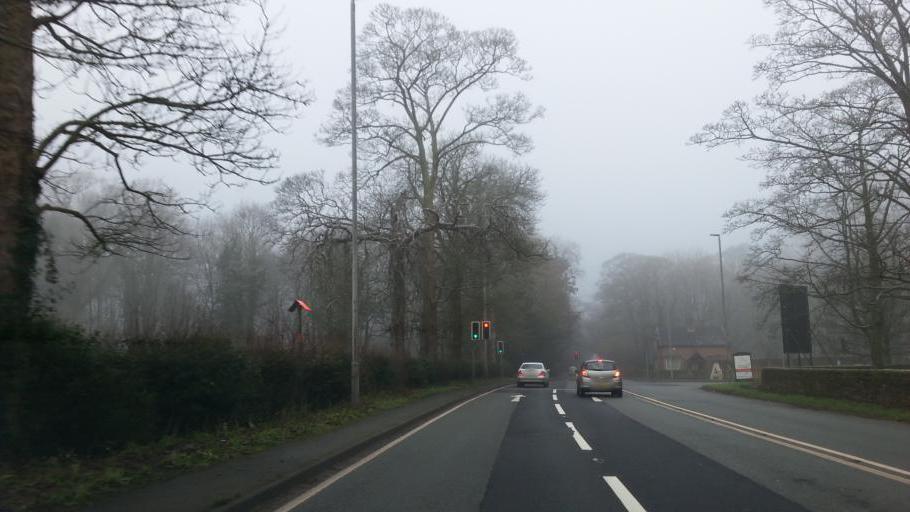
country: GB
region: England
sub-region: Cheshire East
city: Alderley Edge
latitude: 53.2693
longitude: -2.2375
